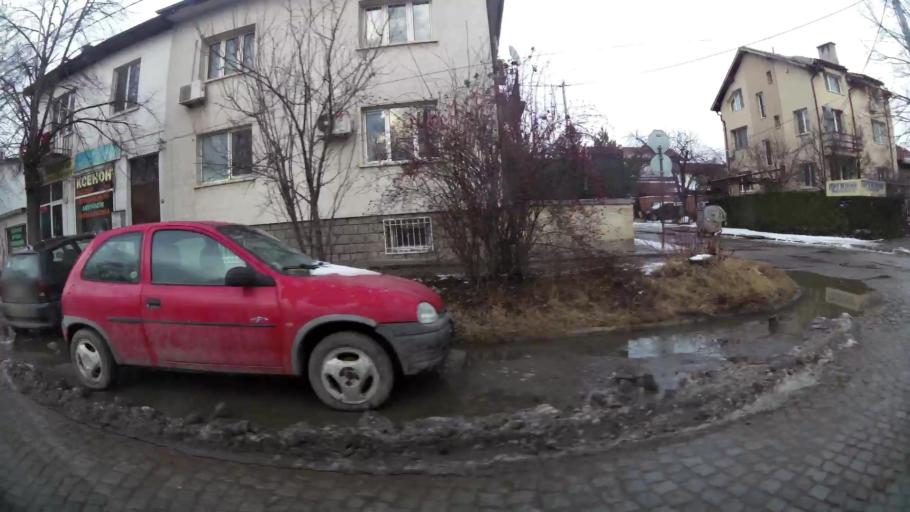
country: BG
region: Sofia-Capital
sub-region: Stolichna Obshtina
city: Sofia
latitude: 42.7202
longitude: 23.3342
